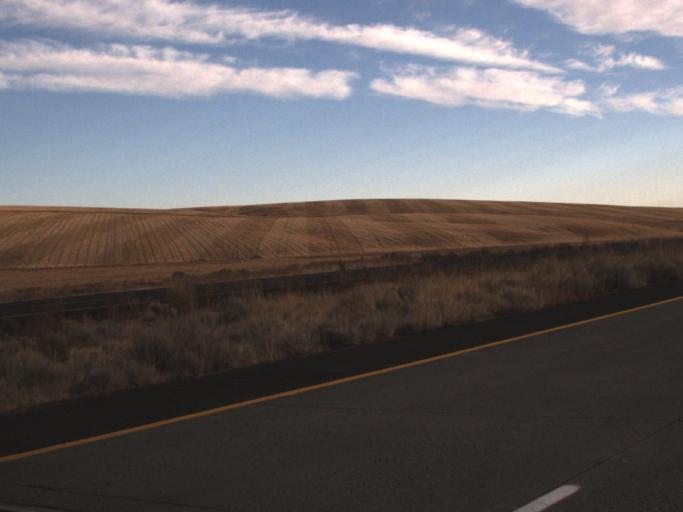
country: US
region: Washington
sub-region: Franklin County
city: Connell
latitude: 46.8309
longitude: -118.6598
